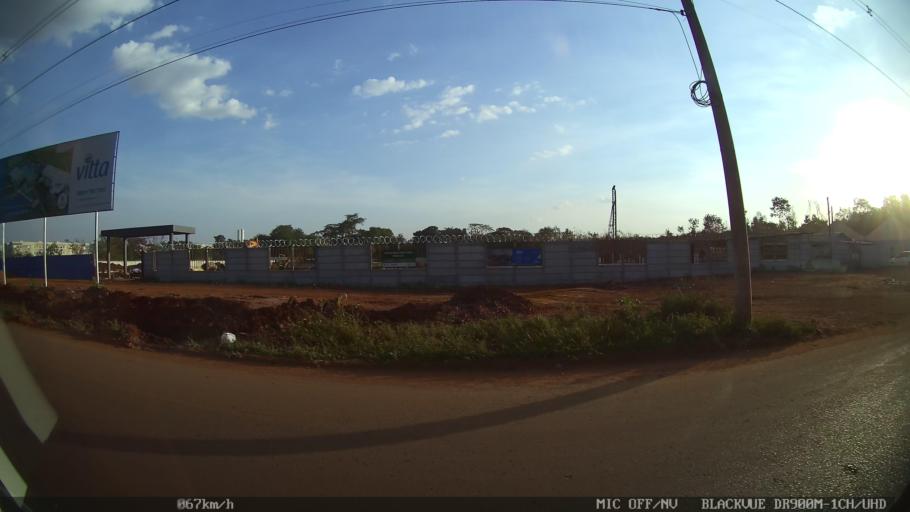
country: BR
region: Sao Paulo
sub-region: Ribeirao Preto
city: Ribeirao Preto
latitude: -21.1144
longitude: -47.8068
